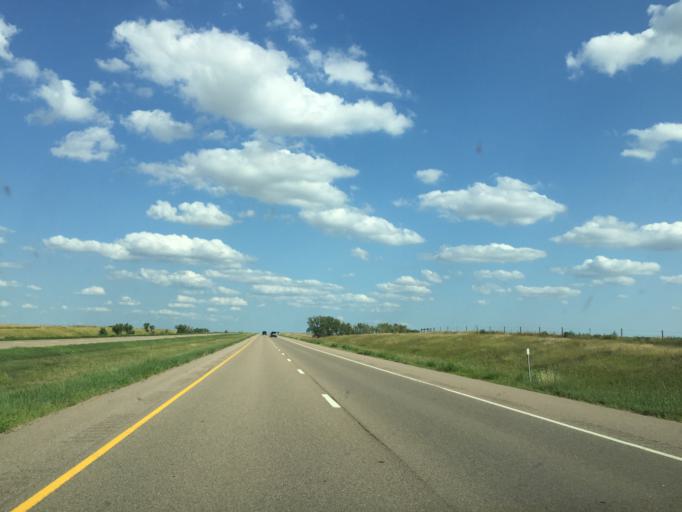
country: US
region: Kansas
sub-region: Gove County
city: Gove
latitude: 39.0933
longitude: -100.3173
